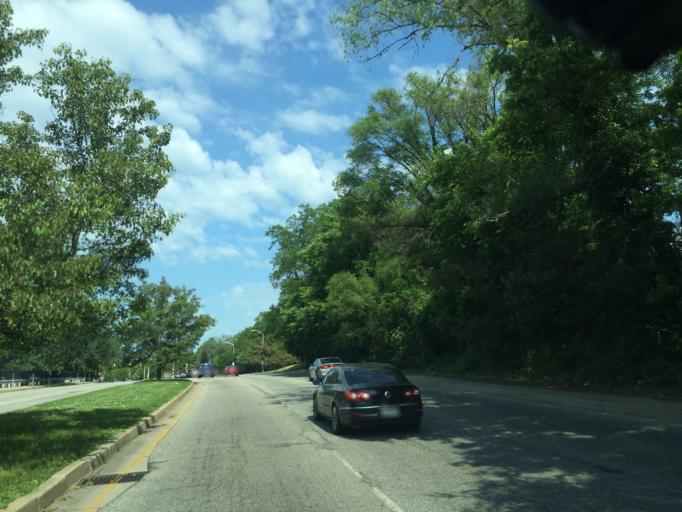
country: US
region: Maryland
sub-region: Baltimore County
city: Towson
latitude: 39.3648
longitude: -76.6072
